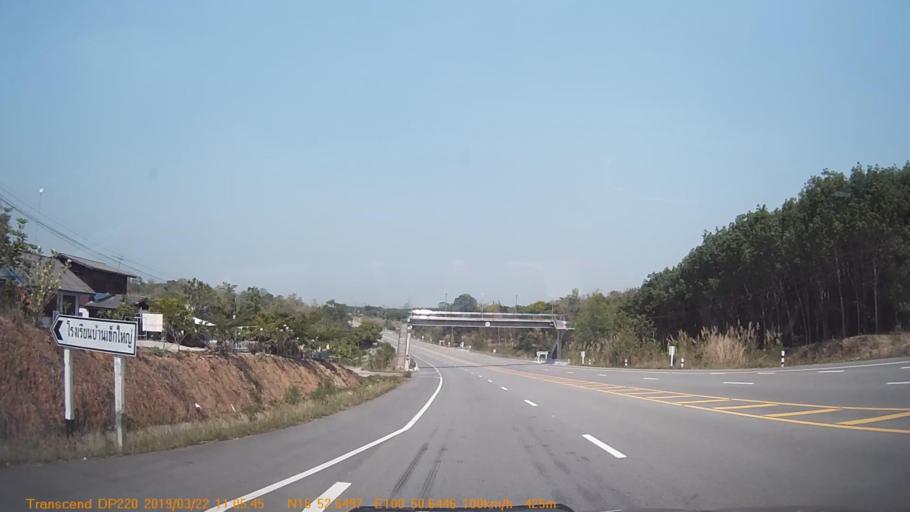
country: TH
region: Phitsanulok
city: Nakhon Thai
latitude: 16.8777
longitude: 100.8439
